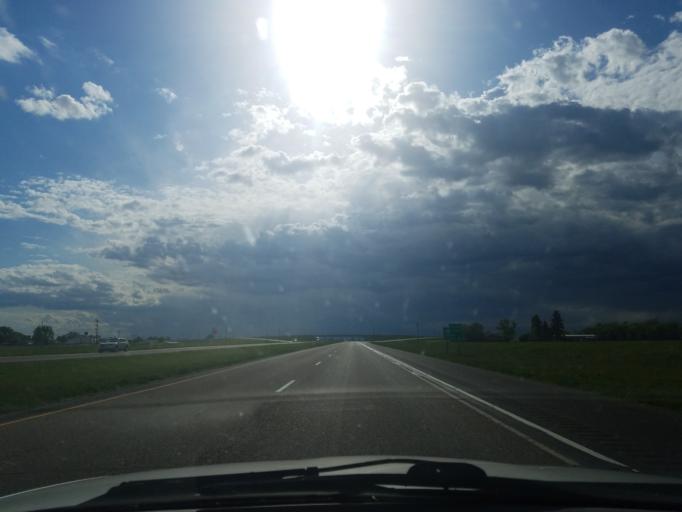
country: US
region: North Dakota
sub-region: Kidder County
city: Steele
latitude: 46.8646
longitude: -99.9074
